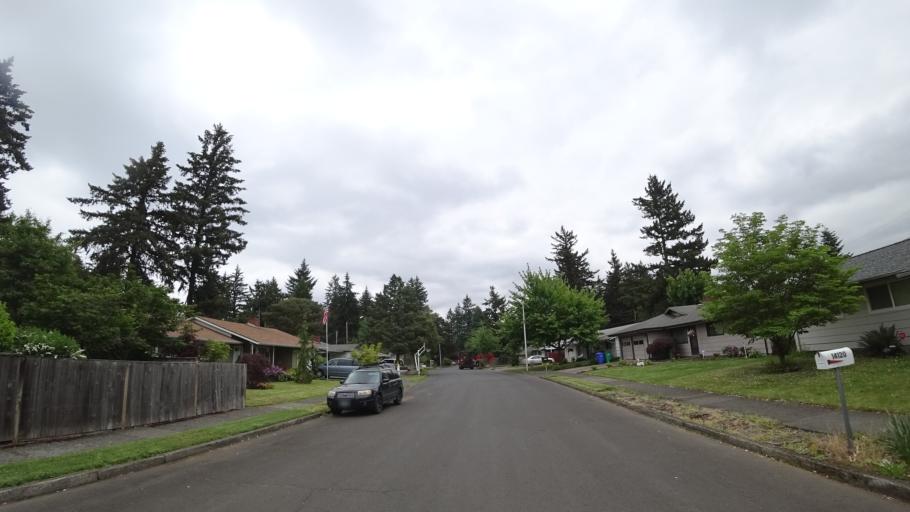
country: US
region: Oregon
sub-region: Multnomah County
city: Lents
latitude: 45.5117
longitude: -122.5182
